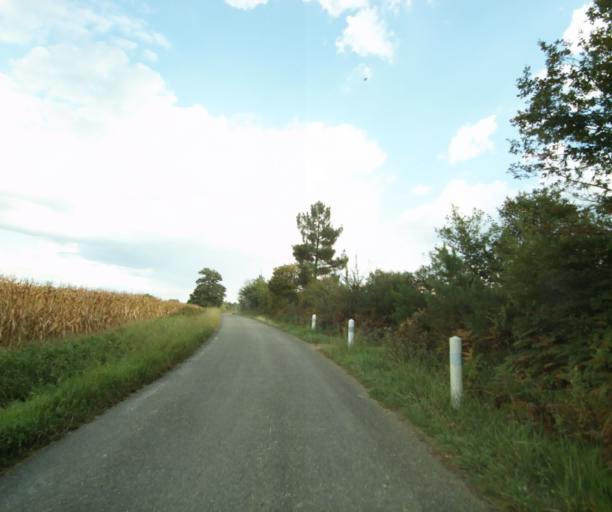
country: FR
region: Midi-Pyrenees
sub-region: Departement du Gers
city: Cazaubon
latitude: 43.9055
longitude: -0.0880
